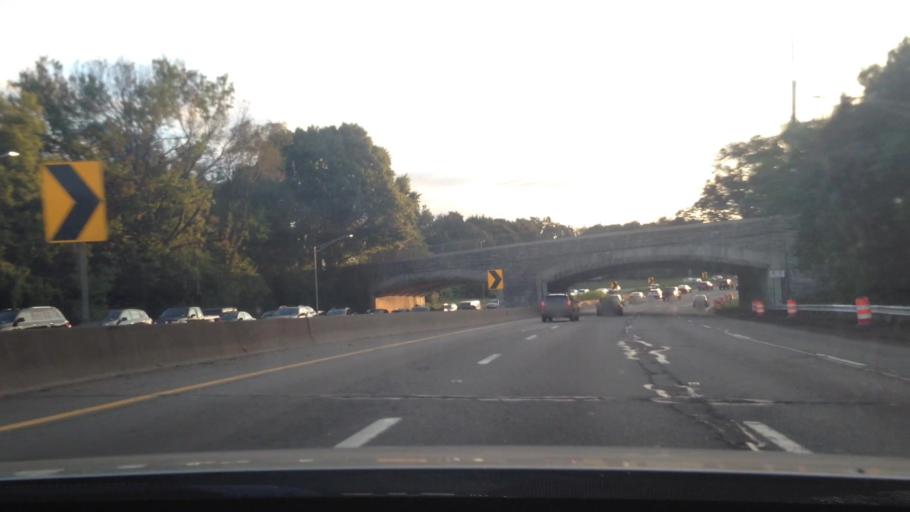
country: US
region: New York
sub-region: Nassau County
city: Elmont
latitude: 40.6877
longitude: -73.7239
